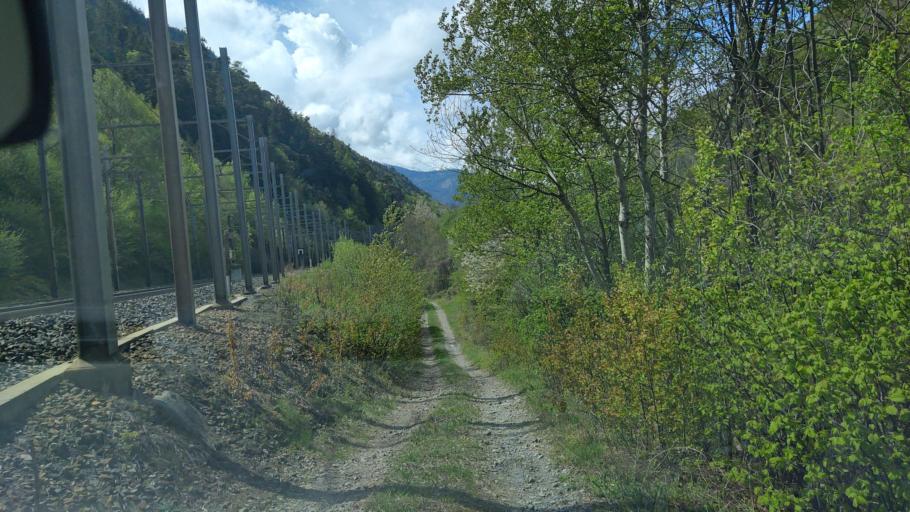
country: FR
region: Rhone-Alpes
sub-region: Departement de la Savoie
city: Saint-Michel-de-Maurienne
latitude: 45.2068
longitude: 6.5279
